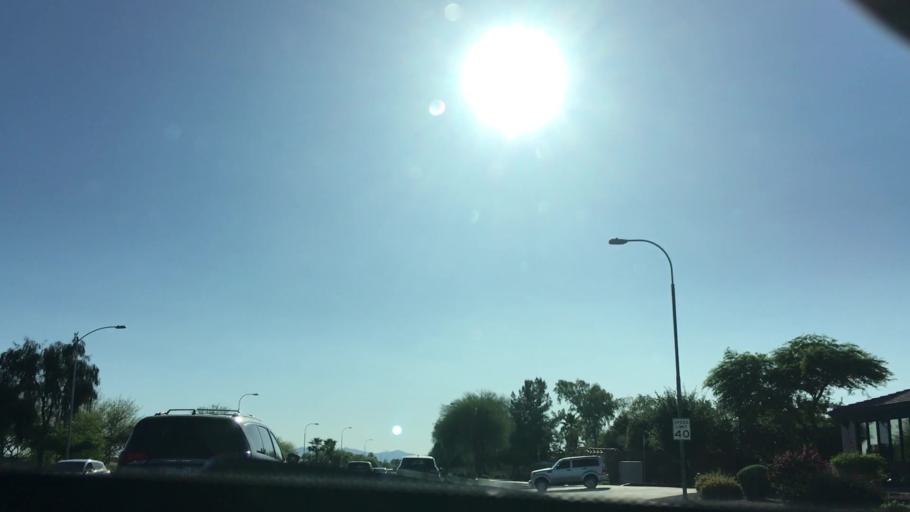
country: US
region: Arizona
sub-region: Maricopa County
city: Peoria
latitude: 33.6106
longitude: -112.2224
